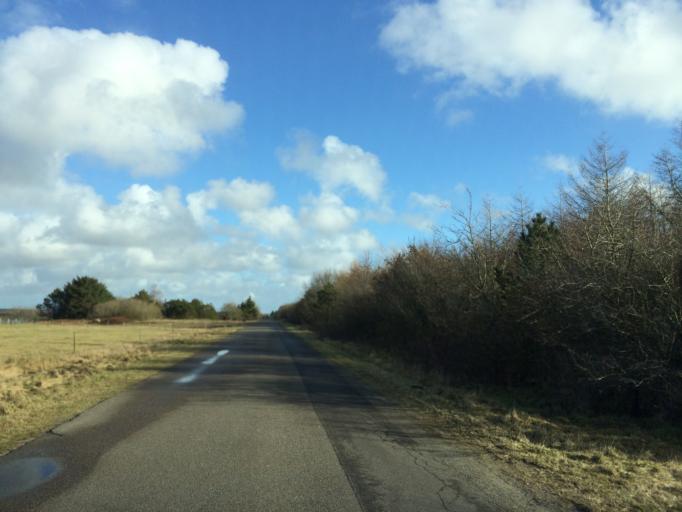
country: DK
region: Central Jutland
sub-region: Holstebro Kommune
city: Ulfborg
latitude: 56.2411
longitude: 8.3962
